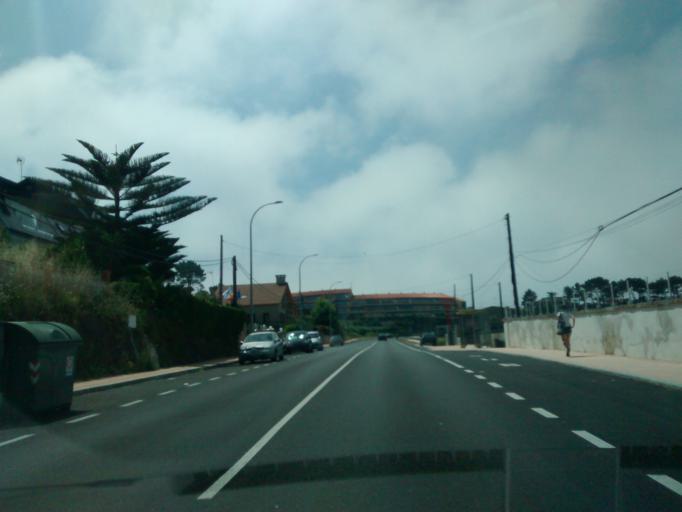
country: ES
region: Galicia
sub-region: Provincia de Pontevedra
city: O Grove
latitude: 42.4272
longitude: -8.8721
